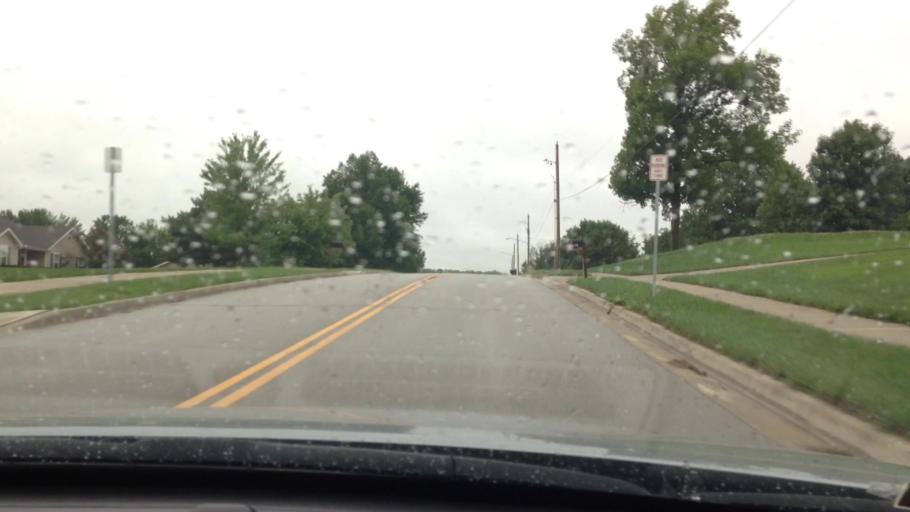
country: US
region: Kansas
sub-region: Leavenworth County
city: Leavenworth
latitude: 39.2885
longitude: -94.9436
